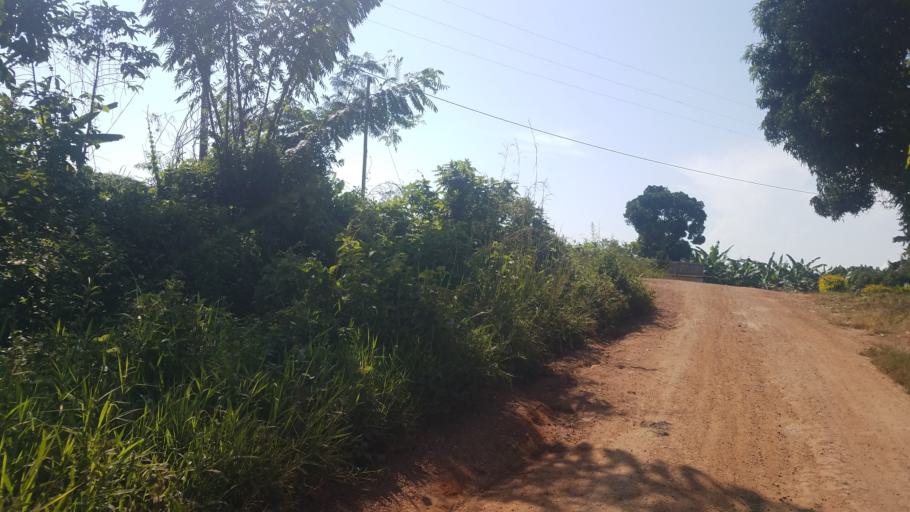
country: UG
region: Central Region
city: Masaka
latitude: -0.3022
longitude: 31.6819
